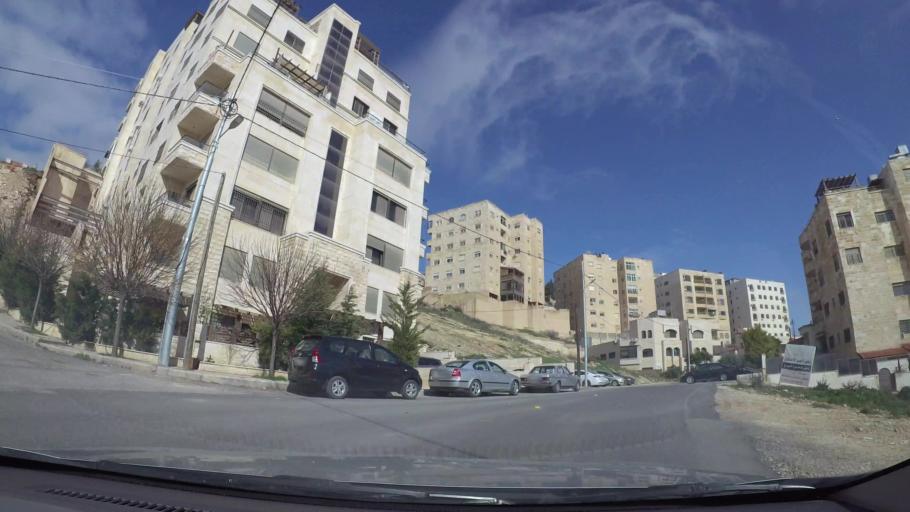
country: JO
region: Amman
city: Al Jubayhah
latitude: 32.0037
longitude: 35.8447
